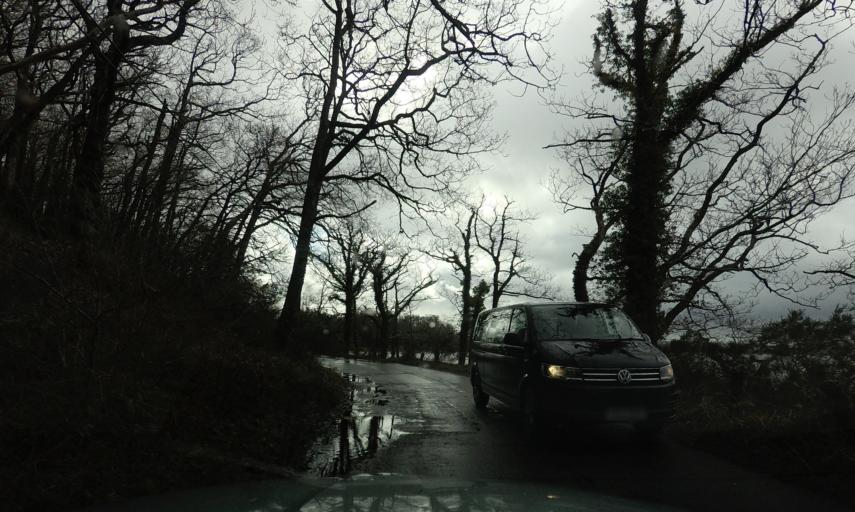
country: GB
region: Scotland
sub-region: West Dunbartonshire
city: Balloch
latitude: 56.1146
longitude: -4.5855
